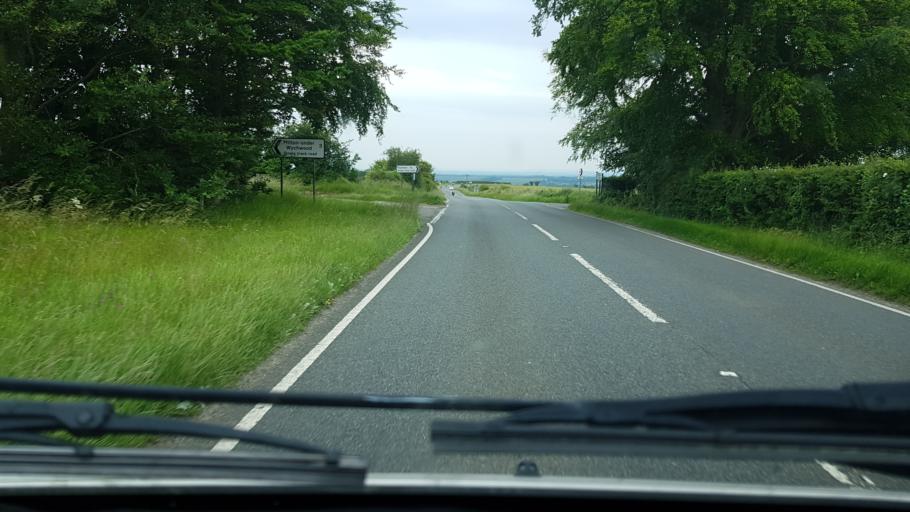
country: GB
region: England
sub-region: Oxfordshire
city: Burford
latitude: 51.8319
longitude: -1.6410
